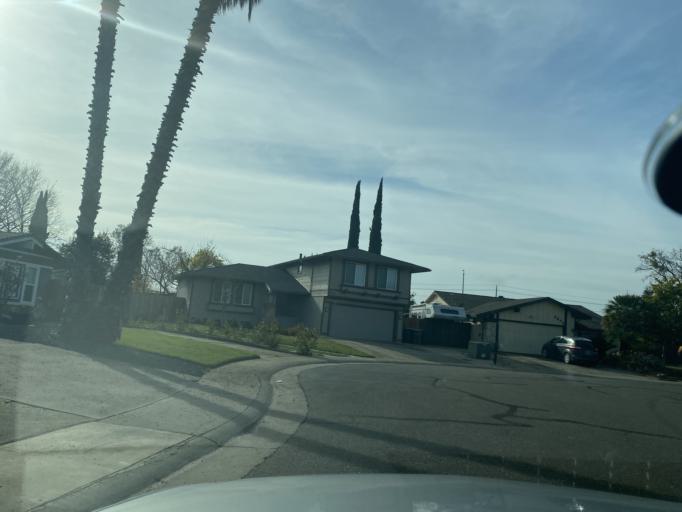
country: US
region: California
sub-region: Sacramento County
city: Elk Grove
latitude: 38.4003
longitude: -121.3816
